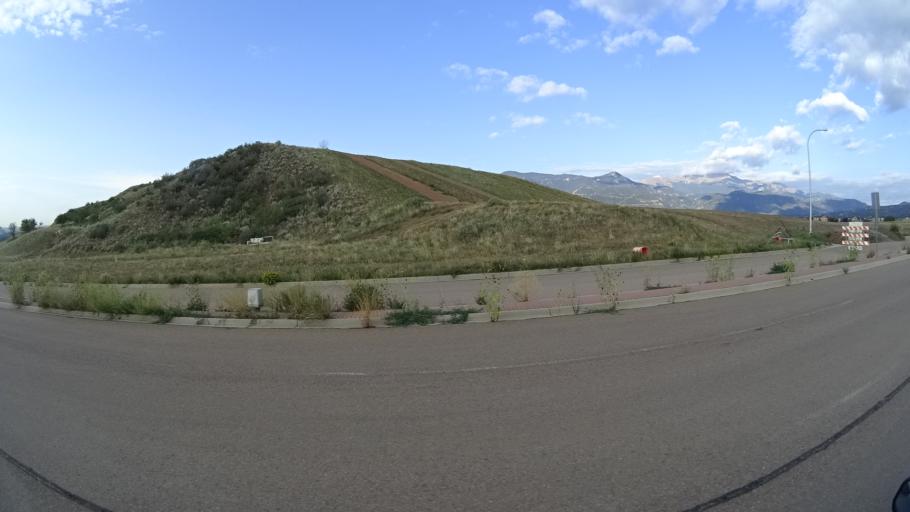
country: US
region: Colorado
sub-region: El Paso County
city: Colorado Springs
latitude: 38.8730
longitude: -104.8436
